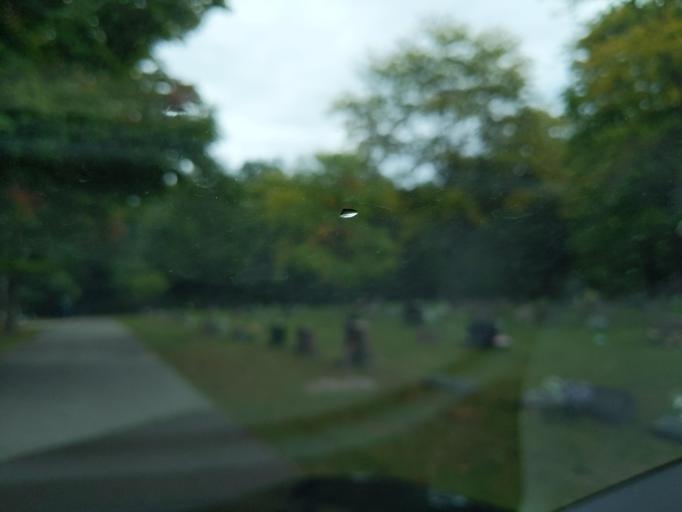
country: US
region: Michigan
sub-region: Grand Traverse County
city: Traverse City
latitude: 44.7563
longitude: -85.5861
